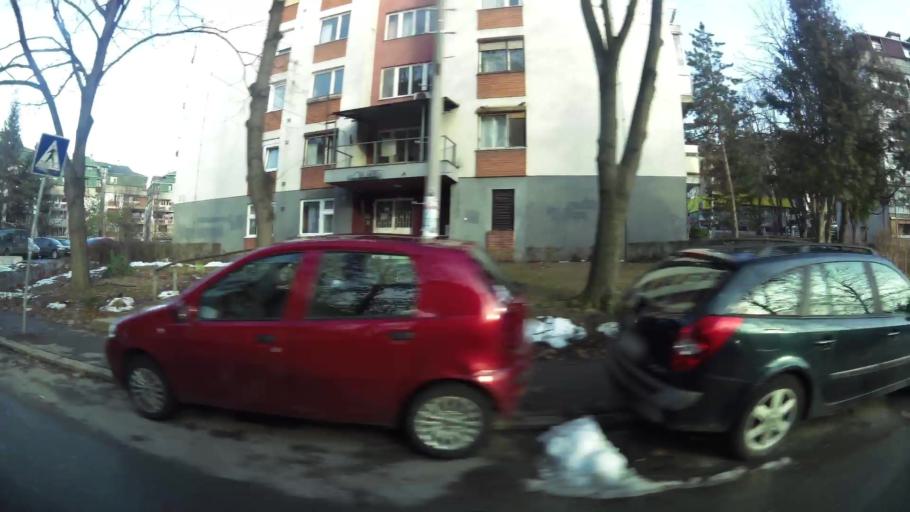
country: RS
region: Central Serbia
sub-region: Belgrade
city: Rakovica
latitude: 44.7460
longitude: 20.4548
